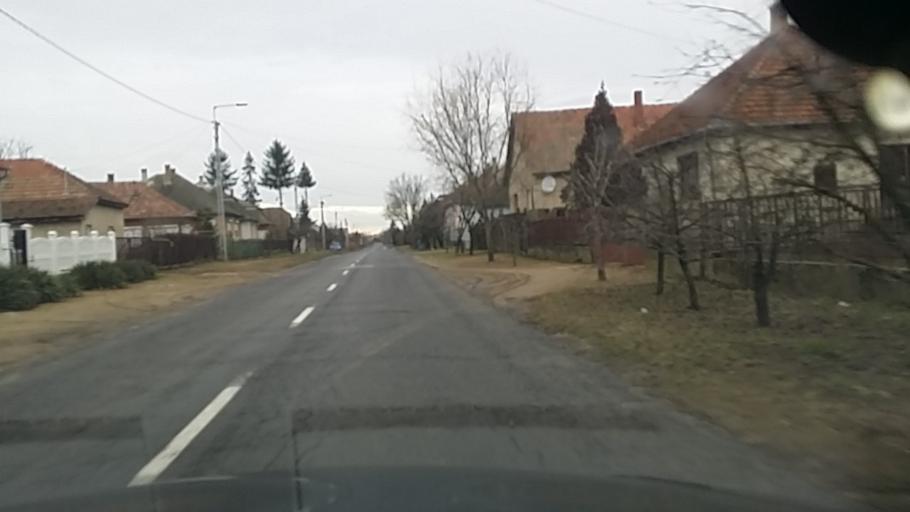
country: HU
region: Szabolcs-Szatmar-Bereg
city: Kek
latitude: 48.1024
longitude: 21.8824
